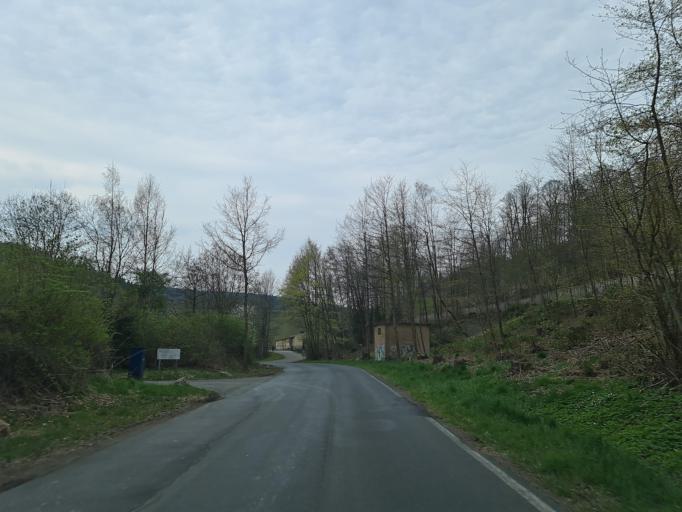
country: DE
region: Saxony
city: Falkenstein
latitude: 50.4700
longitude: 12.3769
